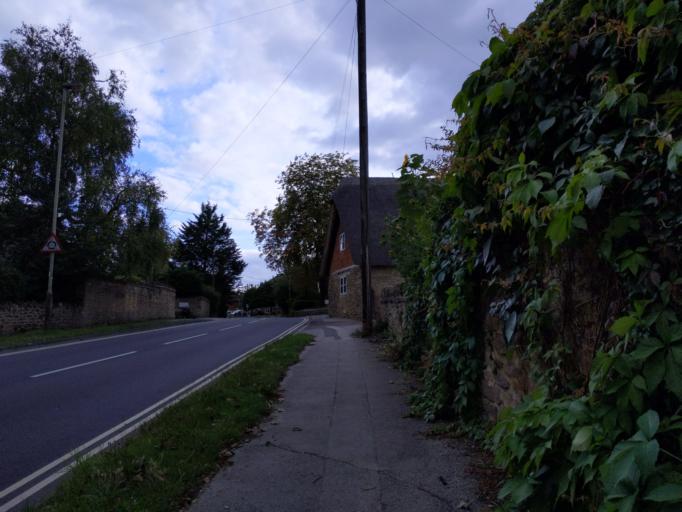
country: GB
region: England
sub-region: Oxfordshire
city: Radley
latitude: 51.7176
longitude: -1.2445
